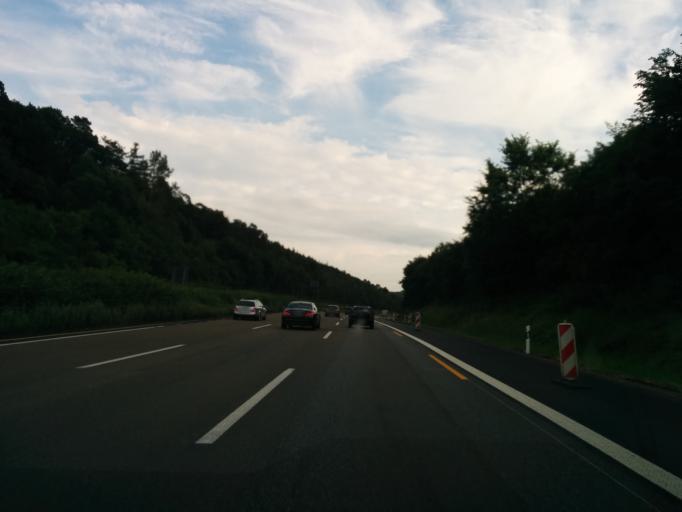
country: DE
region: Hesse
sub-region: Regierungsbezirk Kassel
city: Homberg
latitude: 50.9947
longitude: 9.4736
